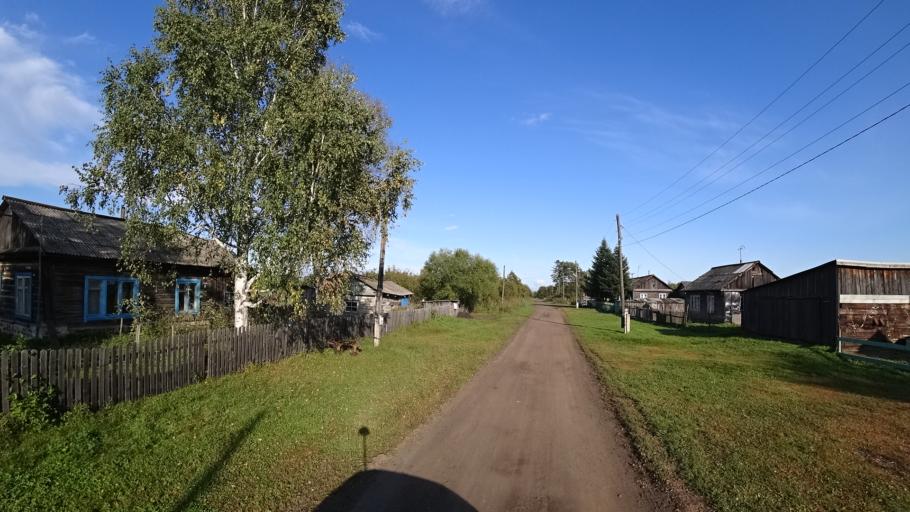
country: RU
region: Amur
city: Arkhara
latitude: 49.3498
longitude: 130.1172
